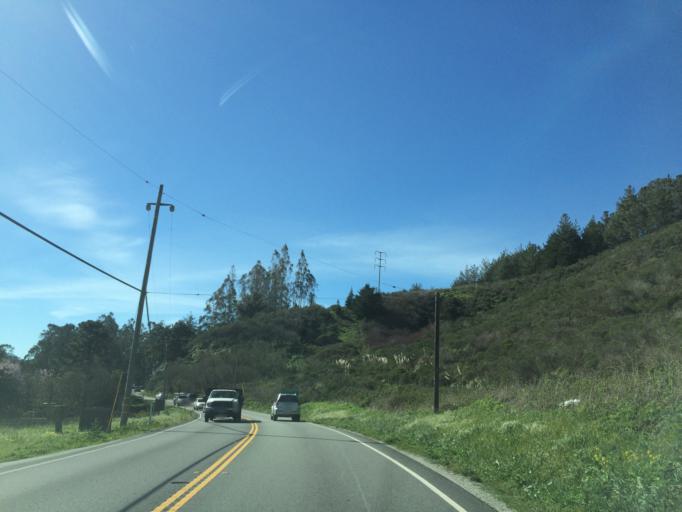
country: US
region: California
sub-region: San Mateo County
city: Half Moon Bay
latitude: 37.4757
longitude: -122.4183
